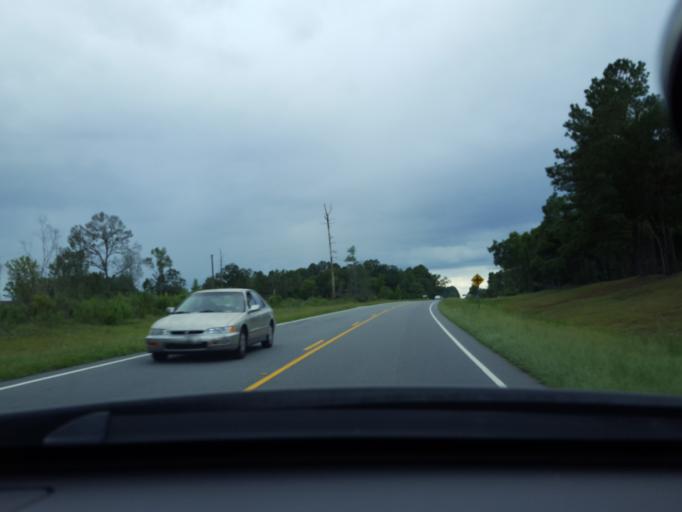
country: US
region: North Carolina
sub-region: Sampson County
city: Roseboro
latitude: 34.7511
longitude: -78.4194
